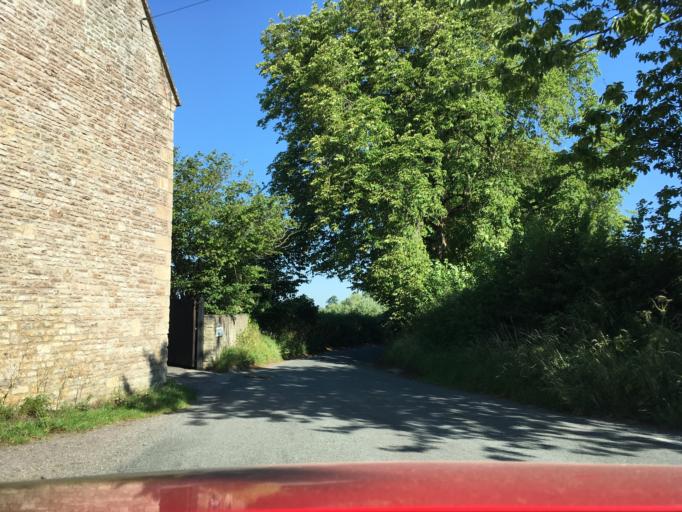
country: GB
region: England
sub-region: South Gloucestershire
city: Hinton
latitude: 51.4791
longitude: -2.3797
